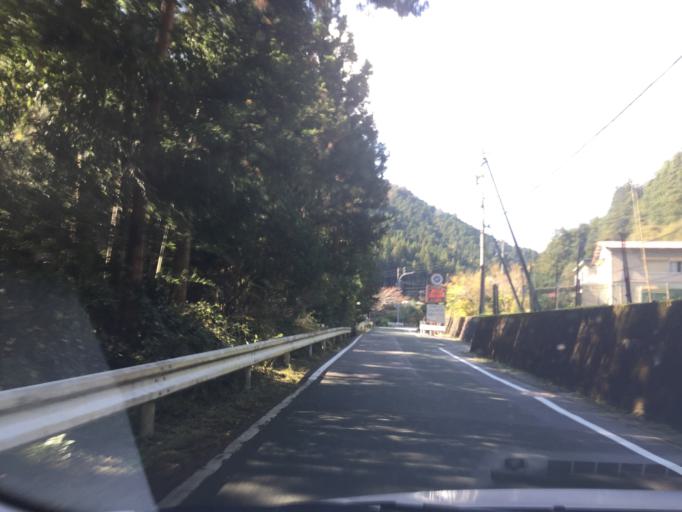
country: JP
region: Aichi
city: Shinshiro
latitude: 35.1192
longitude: 137.6583
